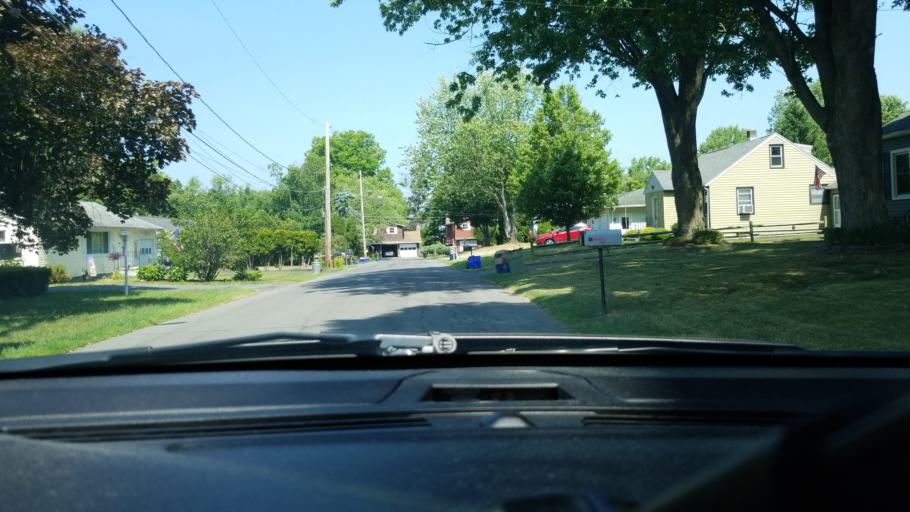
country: US
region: New York
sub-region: Onondaga County
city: Liverpool
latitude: 43.1110
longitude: -76.2225
